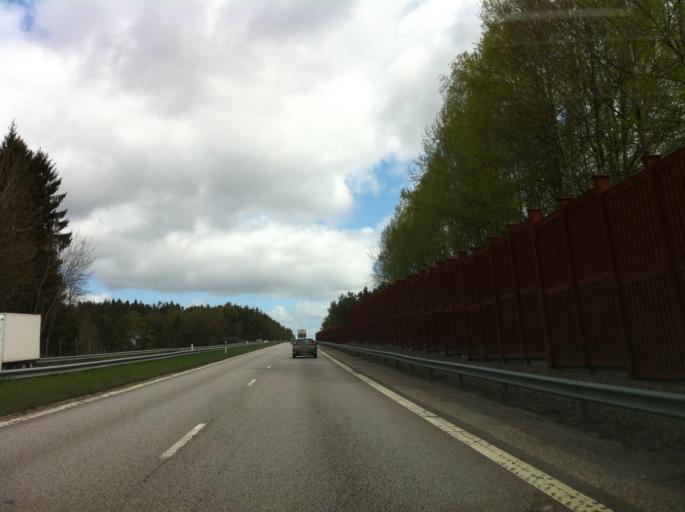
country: SE
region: Vaestra Goetaland
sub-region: Alingsas Kommun
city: Ingared
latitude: 57.8531
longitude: 12.4739
